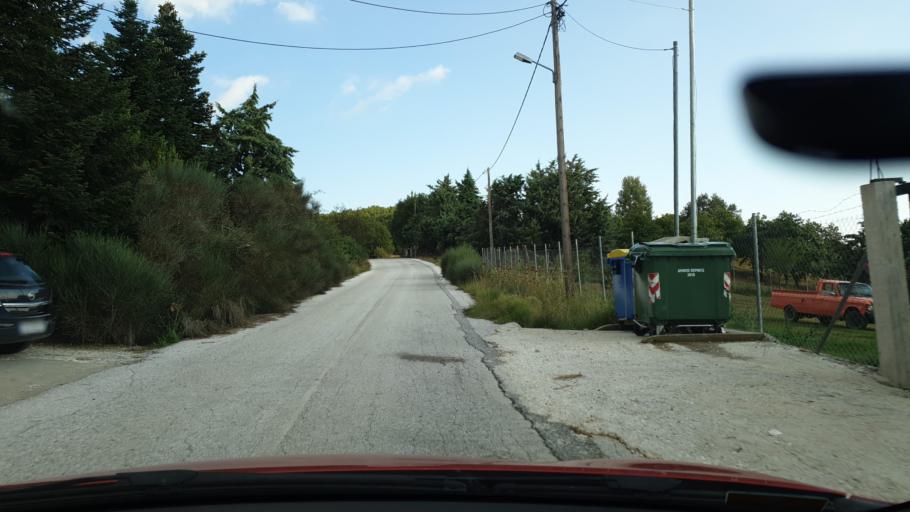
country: GR
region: Central Macedonia
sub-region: Nomos Thessalonikis
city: Peristera
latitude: 40.5190
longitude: 23.2095
